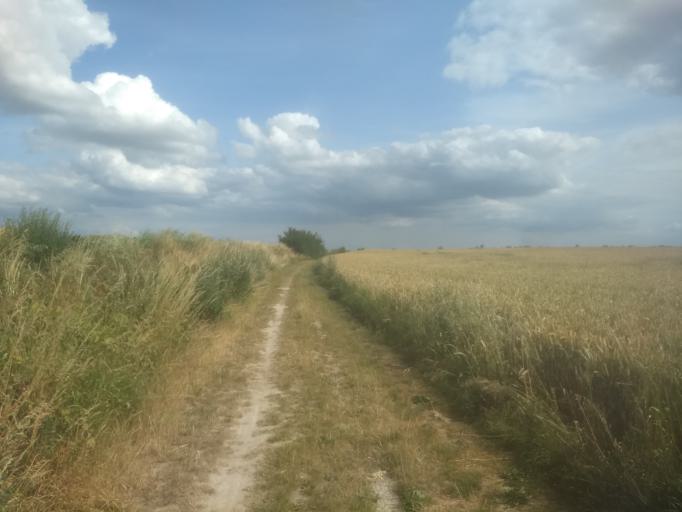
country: FR
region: Nord-Pas-de-Calais
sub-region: Departement du Pas-de-Calais
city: Beaurains
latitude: 50.2752
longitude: 2.7955
